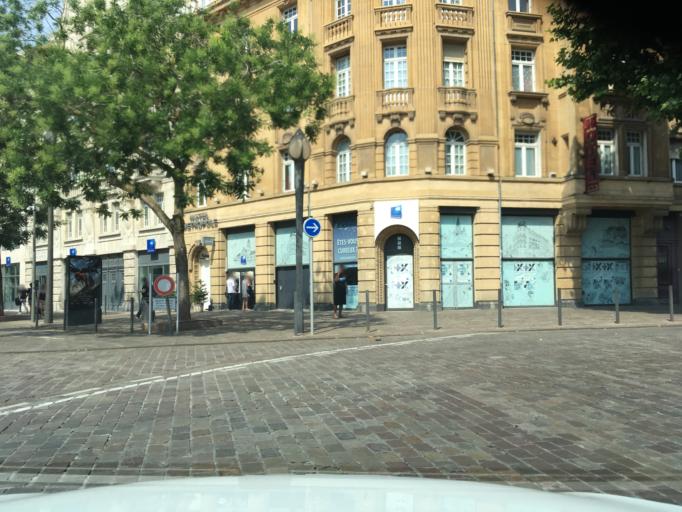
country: FR
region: Lorraine
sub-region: Departement de la Moselle
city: Metz
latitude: 49.1105
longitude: 6.1771
